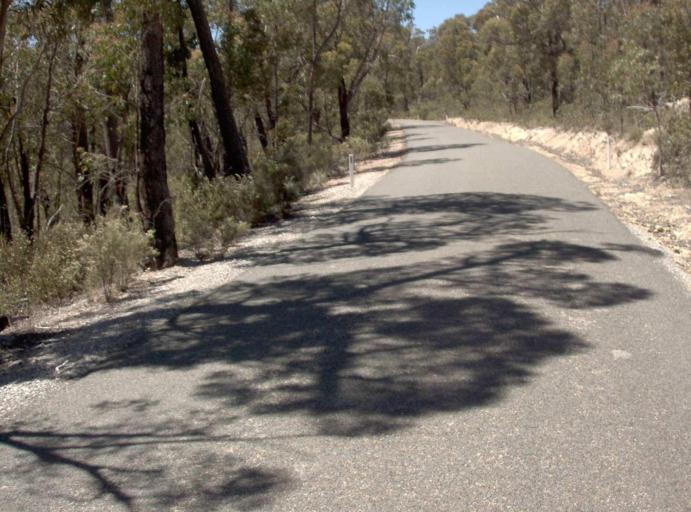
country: AU
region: New South Wales
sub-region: Snowy River
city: Jindabyne
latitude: -37.1213
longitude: 148.2466
